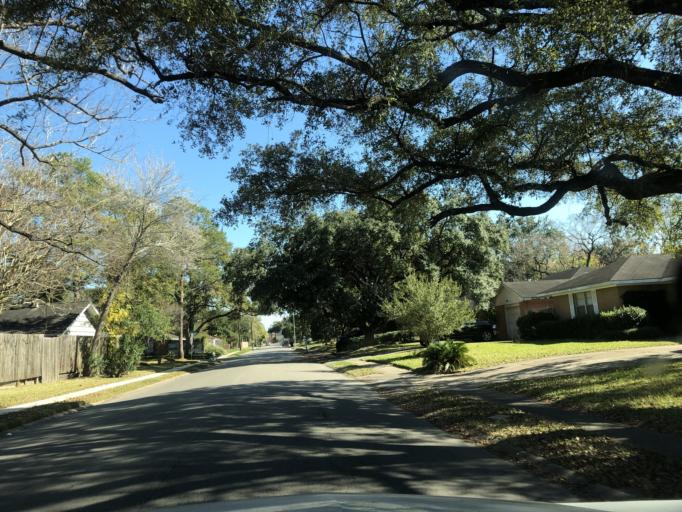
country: US
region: Texas
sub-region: Harris County
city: Bellaire
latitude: 29.6973
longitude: -95.4967
